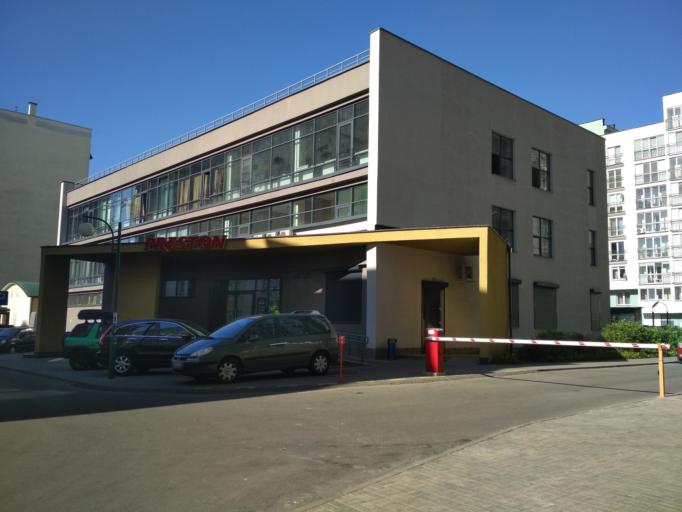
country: BY
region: Minsk
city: Minsk
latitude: 53.8775
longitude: 27.5449
